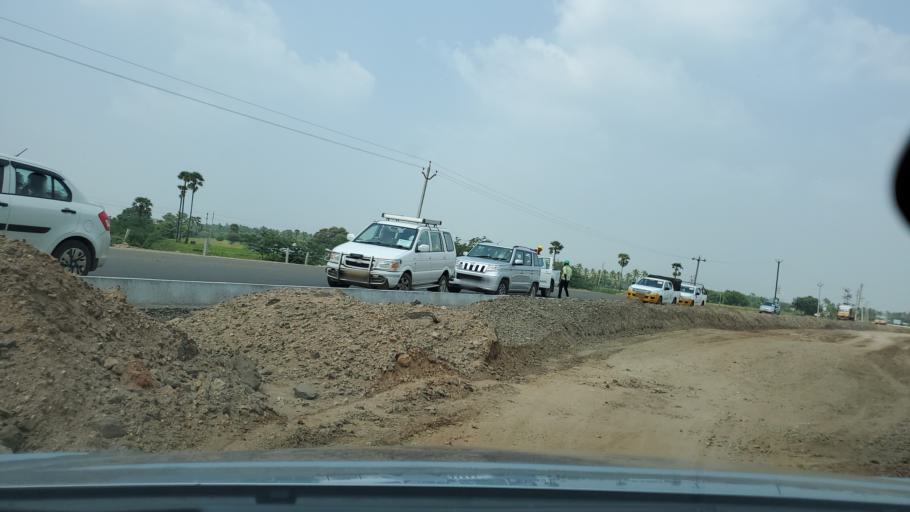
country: IN
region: Tamil Nadu
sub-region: Tiruppur
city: Kangayam
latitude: 10.9176
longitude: 77.4519
